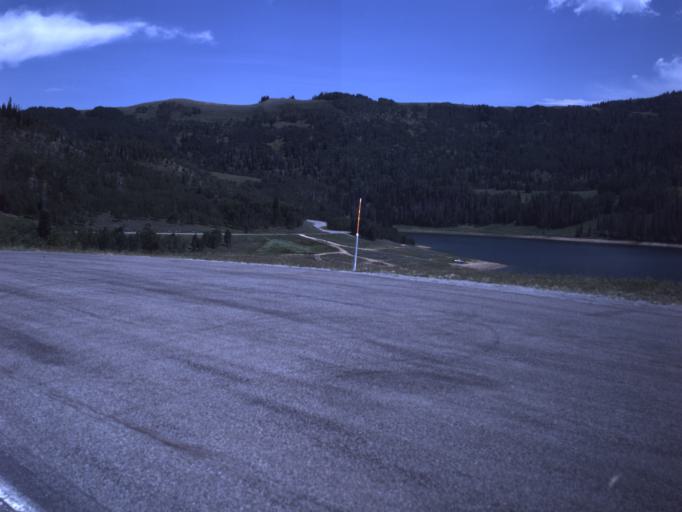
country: US
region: Utah
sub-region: Sanpete County
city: Fairview
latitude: 39.5833
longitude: -111.2429
